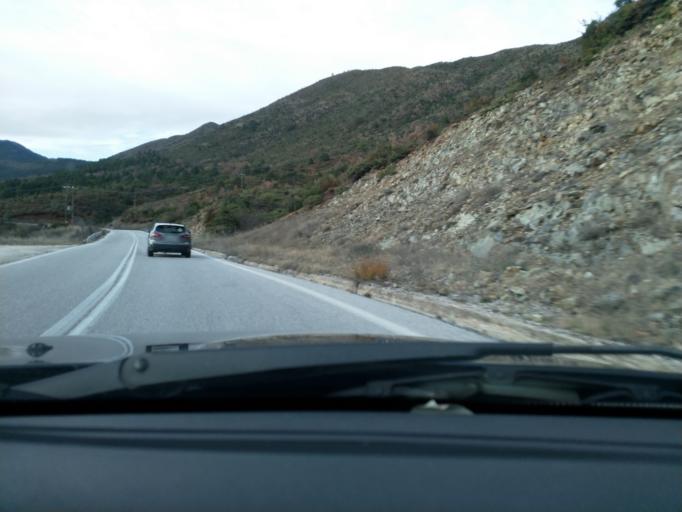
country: GR
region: Thessaly
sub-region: Trikala
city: Kastraki
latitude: 39.7749
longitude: 21.4520
